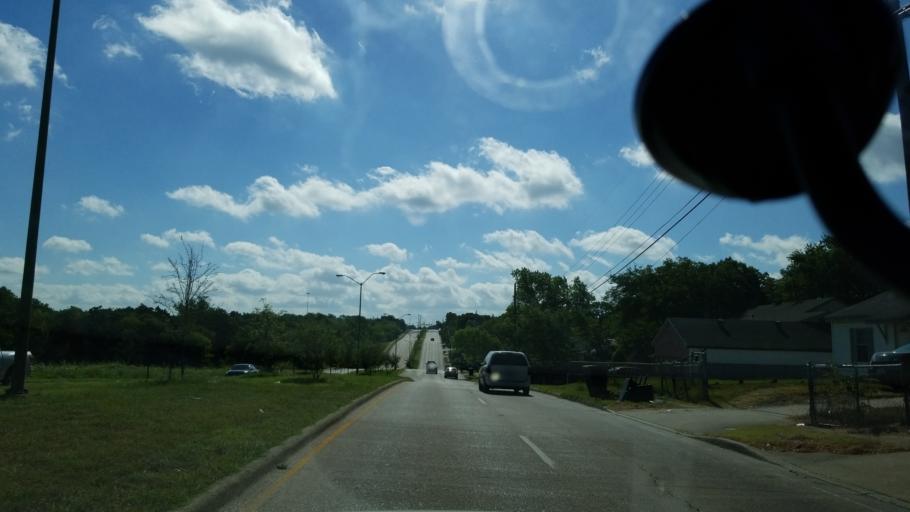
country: US
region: Texas
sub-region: Dallas County
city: Duncanville
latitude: 32.6747
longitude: -96.8307
